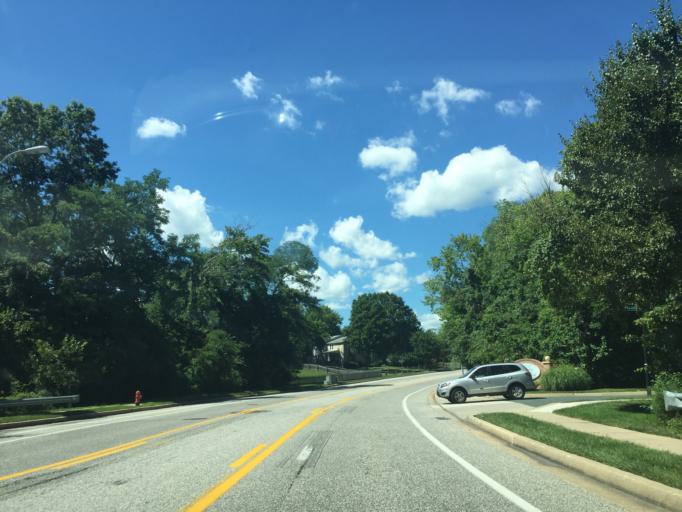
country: US
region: Maryland
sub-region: Baltimore County
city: Perry Hall
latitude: 39.4015
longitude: -76.4858
